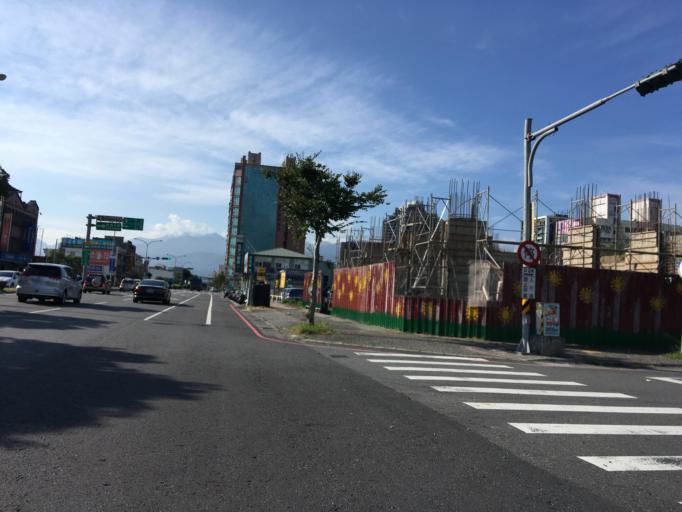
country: TW
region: Taiwan
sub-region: Yilan
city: Yilan
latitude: 24.6793
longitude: 121.7777
